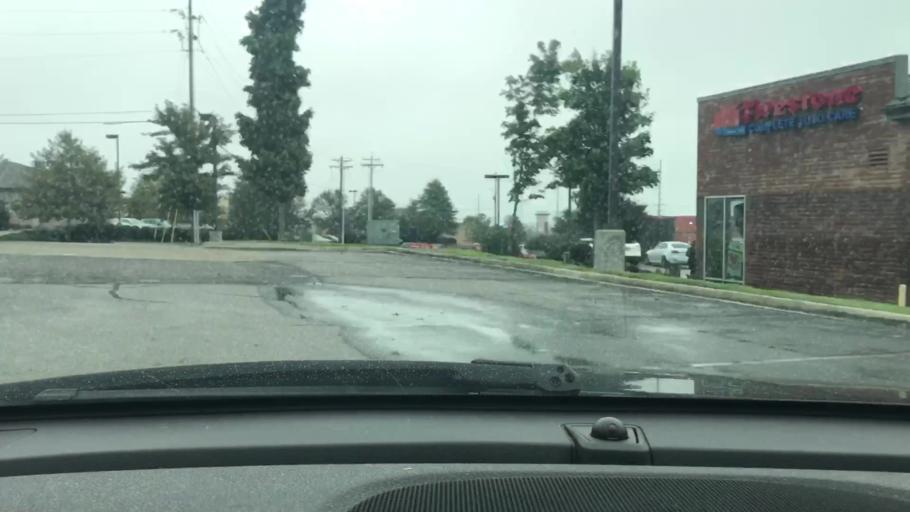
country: US
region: Tennessee
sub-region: Rutherford County
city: La Vergne
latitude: 35.9781
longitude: -86.5669
